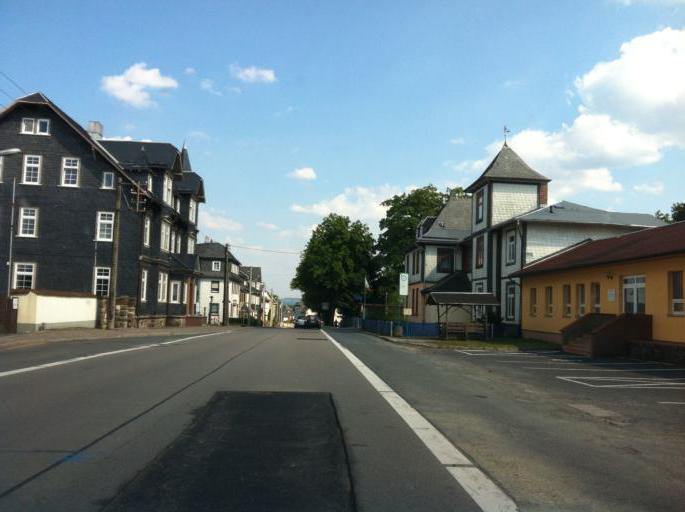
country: DE
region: Thuringia
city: Grossbreitenbach
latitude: 50.5809
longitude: 11.0007
